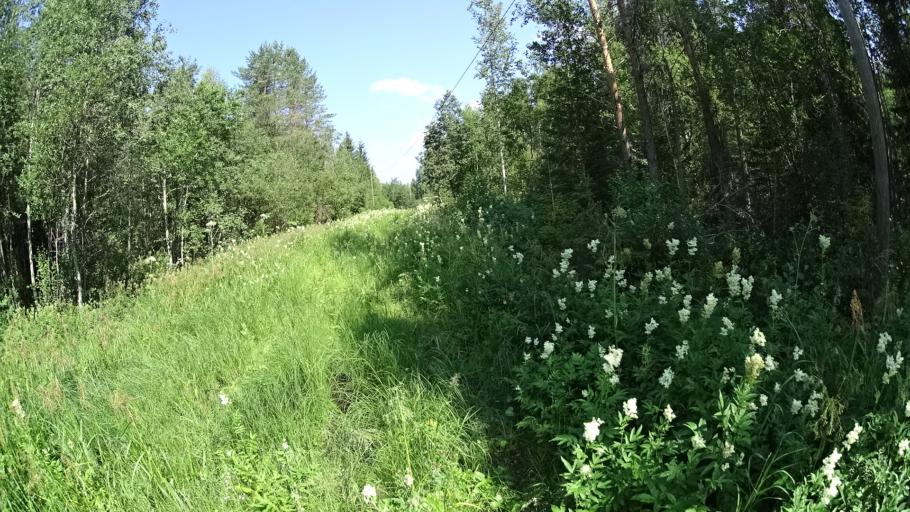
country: FI
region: North Karelia
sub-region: Pielisen Karjala
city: Lieksa
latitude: 63.1179
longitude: 29.7929
